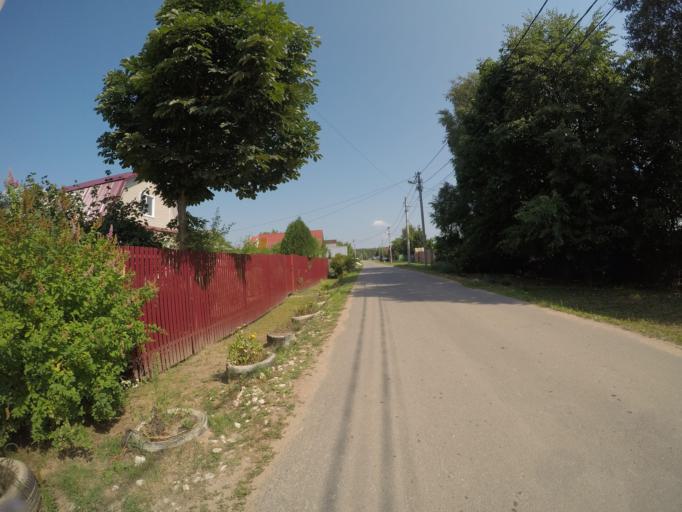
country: RU
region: Moskovskaya
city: Rechitsy
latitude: 55.6371
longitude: 38.5081
